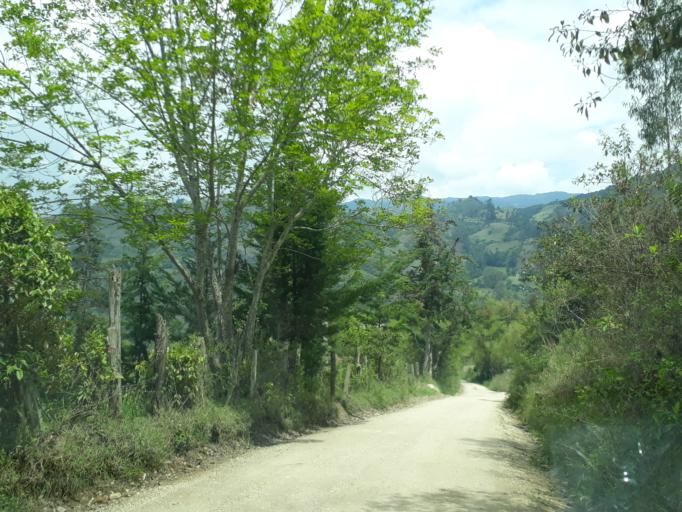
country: CO
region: Cundinamarca
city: Macheta
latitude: 5.0933
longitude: -73.5625
